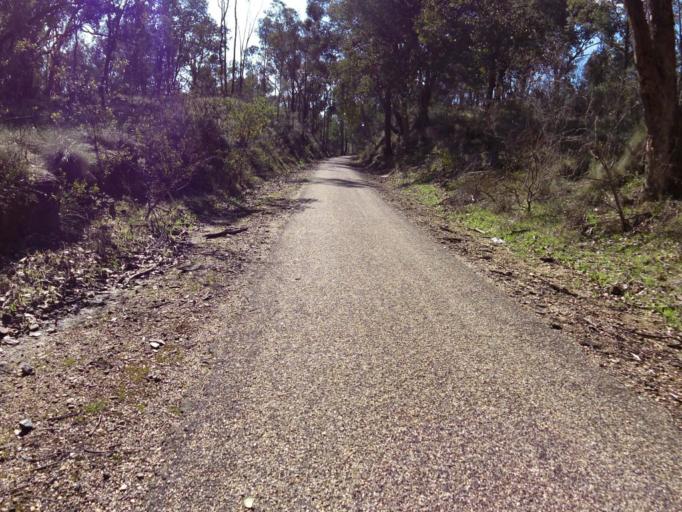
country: AU
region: Victoria
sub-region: Wangaratta
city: Wangaratta
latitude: -36.4070
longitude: 146.6188
